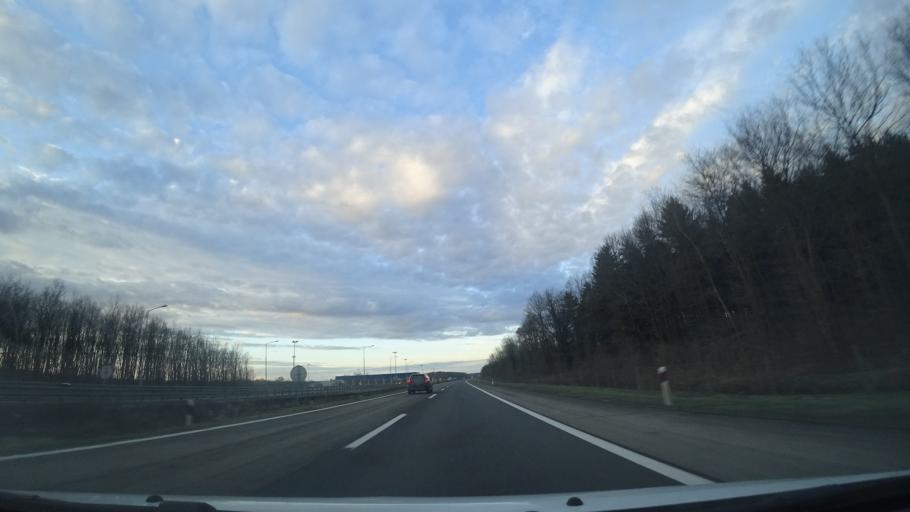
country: HR
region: Grad Zagreb
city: Brezovica
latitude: 45.7263
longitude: 15.8713
